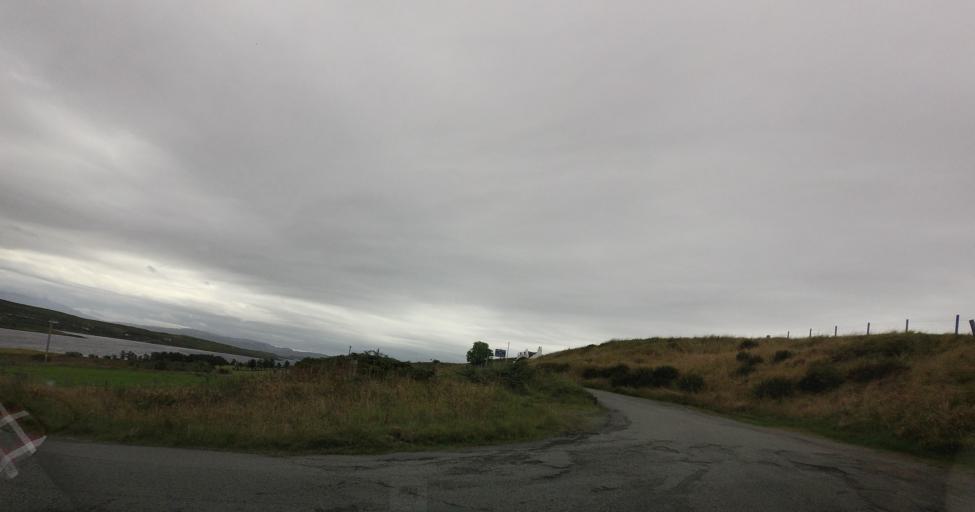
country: GB
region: Scotland
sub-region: Highland
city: Isle of Skye
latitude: 57.4052
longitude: -6.4973
